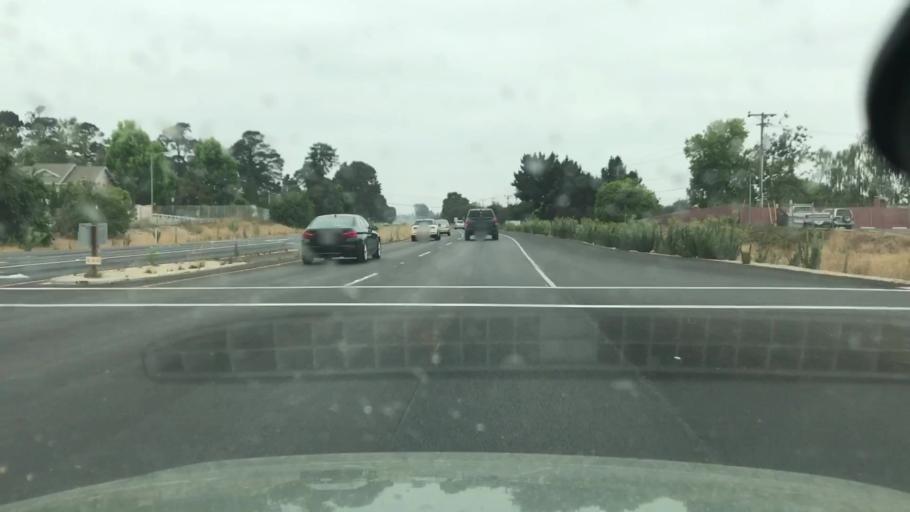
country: US
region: California
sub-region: Santa Barbara County
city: Orcutt
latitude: 34.8993
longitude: -120.4360
